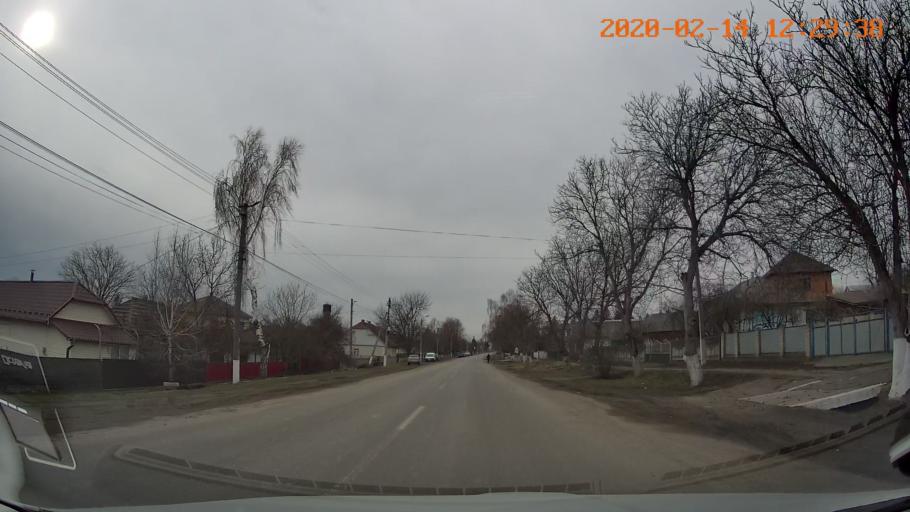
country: RO
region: Botosani
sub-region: Comuna Darabani
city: Bajura
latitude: 48.2559
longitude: 26.5790
